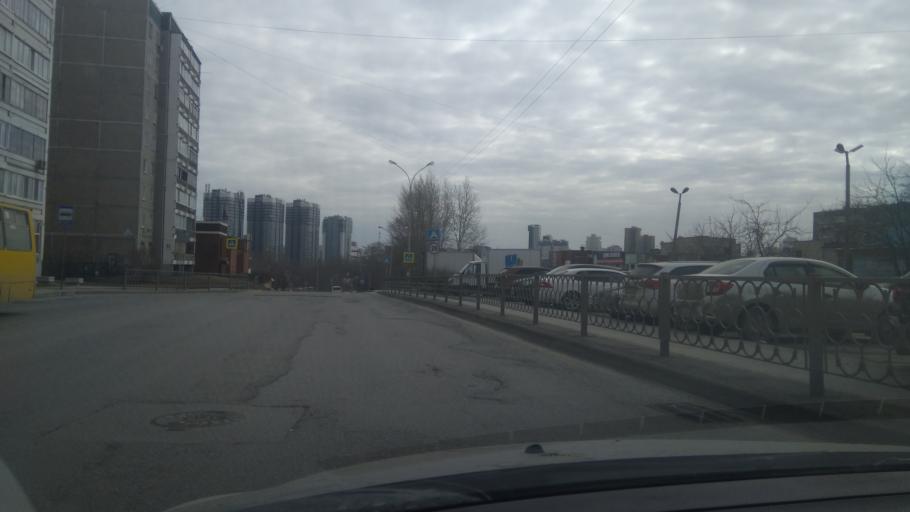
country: RU
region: Sverdlovsk
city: Yekaterinburg
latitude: 56.8501
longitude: 60.5643
